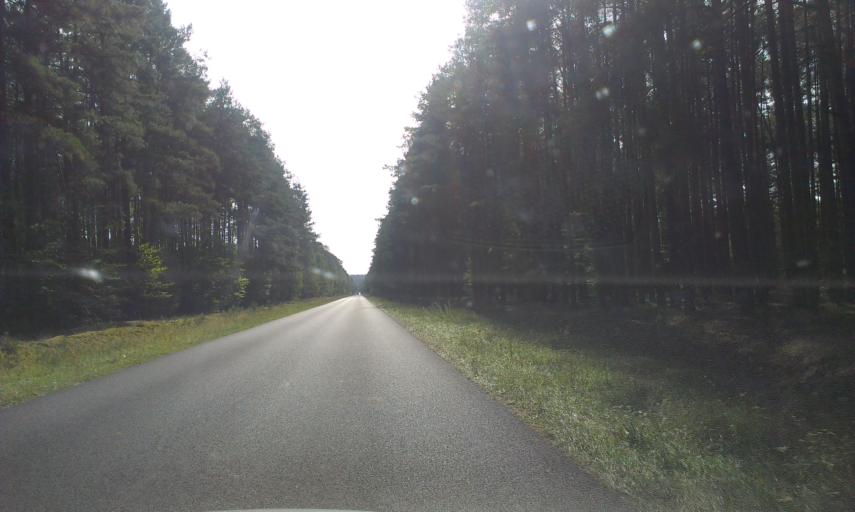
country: PL
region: Greater Poland Voivodeship
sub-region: Powiat zlotowski
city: Okonek
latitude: 53.5118
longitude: 16.9757
